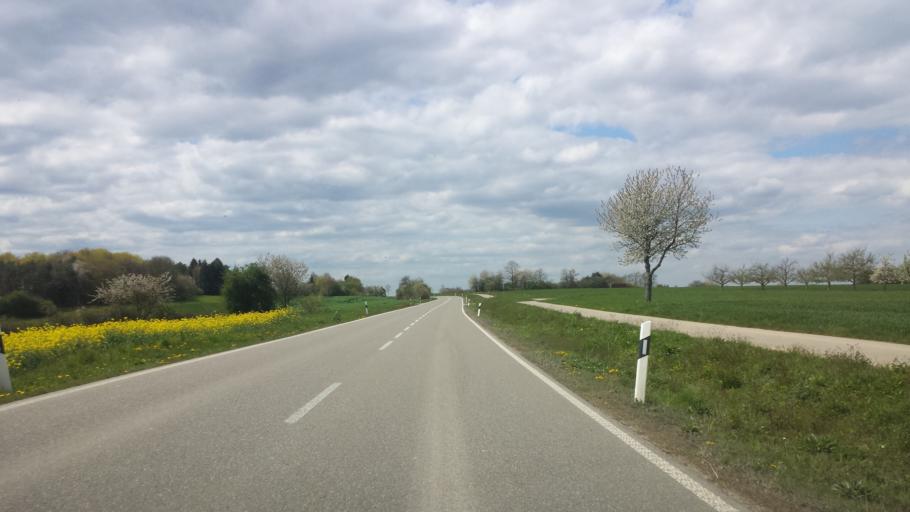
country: DE
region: Baden-Wuerttemberg
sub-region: Karlsruhe Region
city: Monsheim
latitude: 48.8574
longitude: 8.8881
